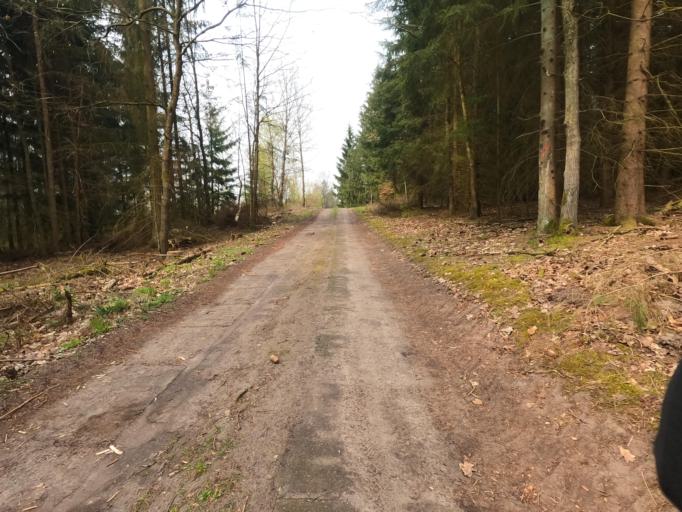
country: PL
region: West Pomeranian Voivodeship
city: Trzcinsko Zdroj
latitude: 52.9126
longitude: 14.5671
